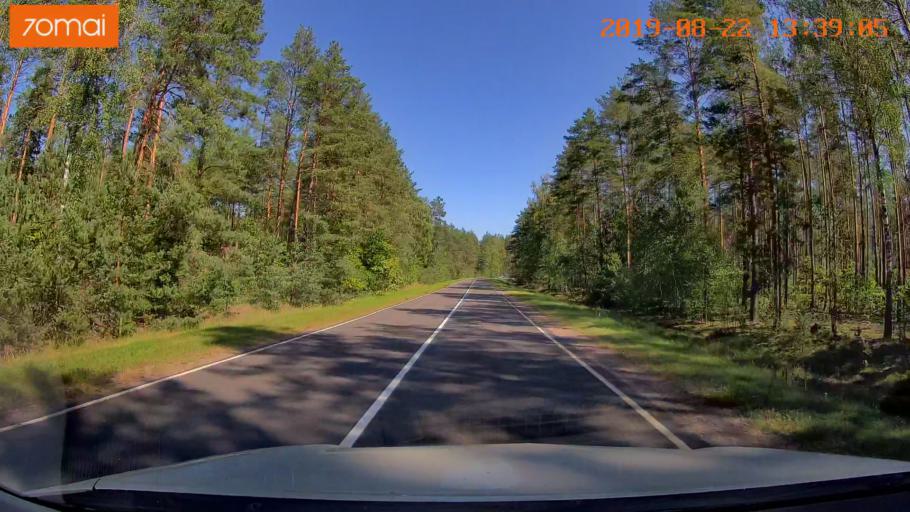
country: BY
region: Minsk
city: Staryya Darohi
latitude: 53.2273
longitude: 28.3408
